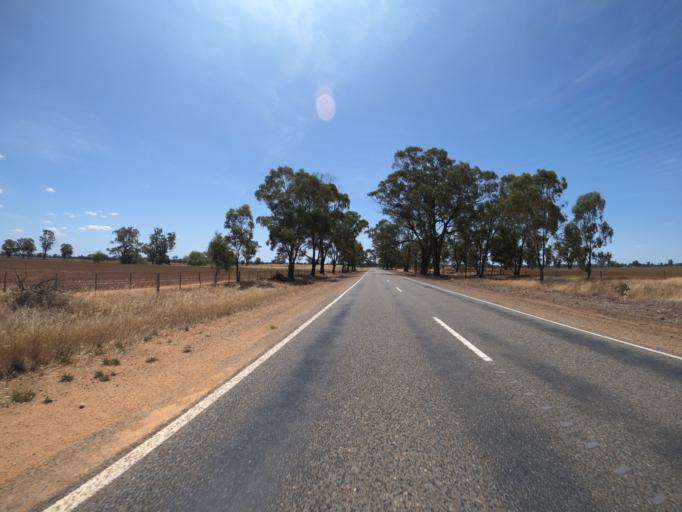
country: AU
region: Victoria
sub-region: Moira
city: Yarrawonga
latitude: -36.1954
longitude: 145.9670
